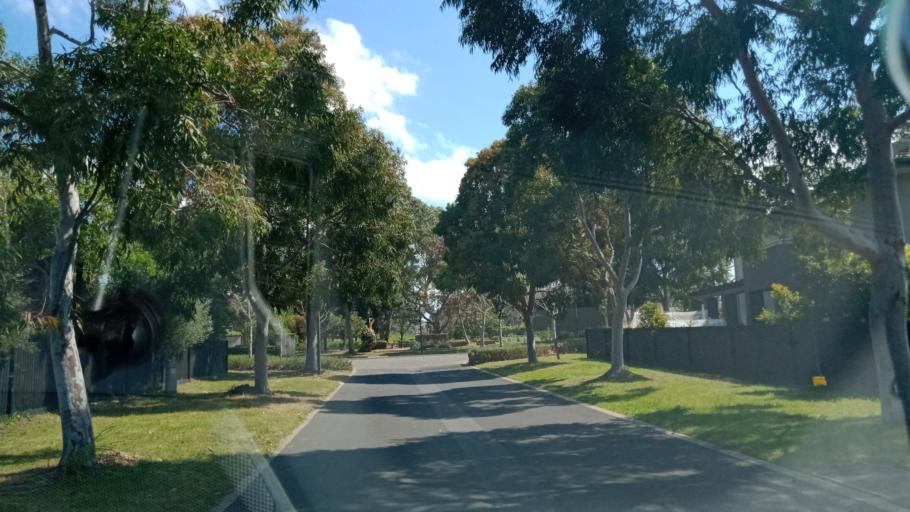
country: AU
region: Victoria
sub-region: Frankston
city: Sandhurst
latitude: -38.0814
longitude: 145.2048
